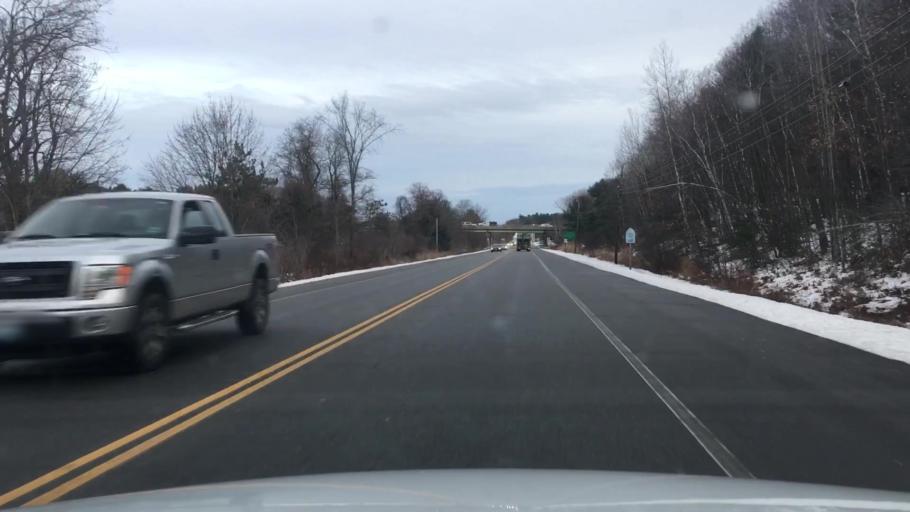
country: US
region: Maine
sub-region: Cumberland County
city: Falmouth Foreside
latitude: 43.7671
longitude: -70.2039
